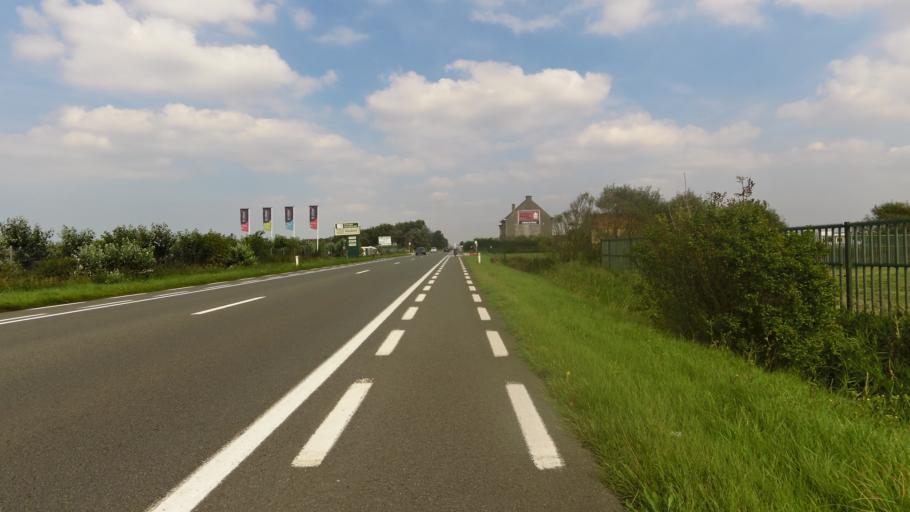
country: BE
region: Flanders
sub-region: Provincie West-Vlaanderen
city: Middelkerke
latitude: 51.1976
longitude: 2.8489
